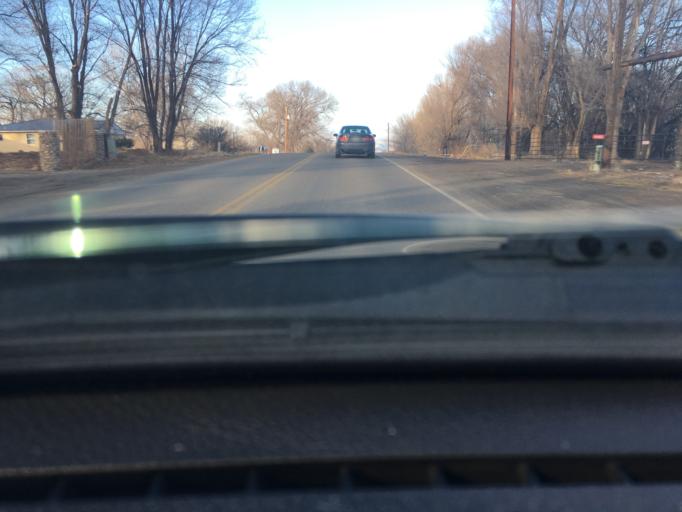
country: US
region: Colorado
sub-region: Delta County
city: Delta
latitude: 38.7410
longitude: -108.0922
